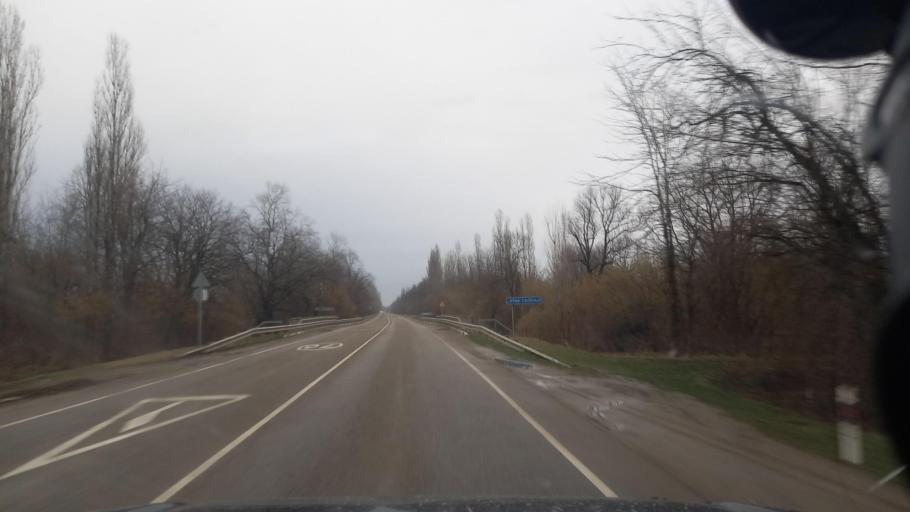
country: RU
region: Krasnodarskiy
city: Saratovskaya
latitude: 44.6791
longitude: 39.2074
